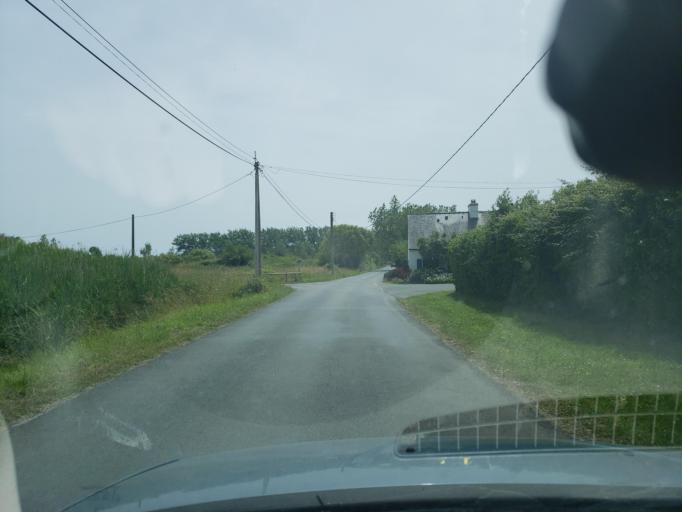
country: FR
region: Brittany
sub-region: Departement du Finistere
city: Guilvinec
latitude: 47.8084
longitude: -4.3198
